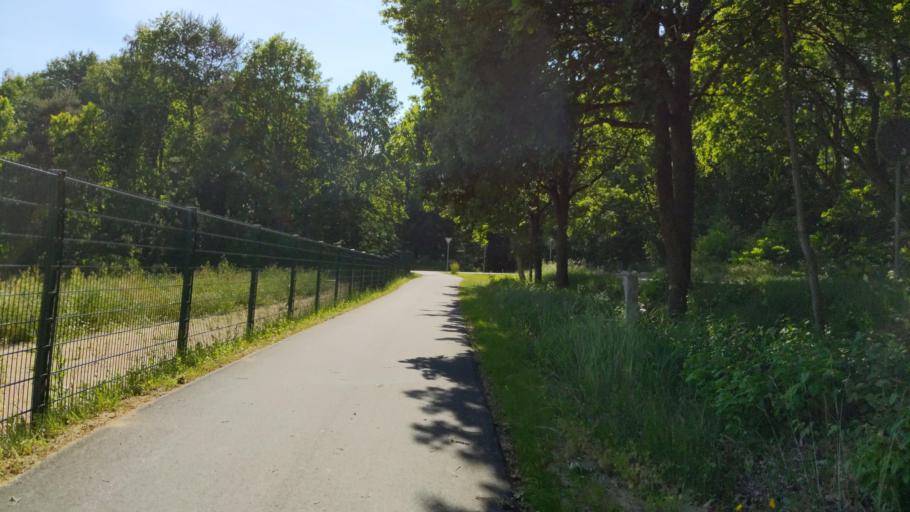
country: DE
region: Schleswig-Holstein
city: Gross Gronau
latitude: 53.8020
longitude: 10.7311
